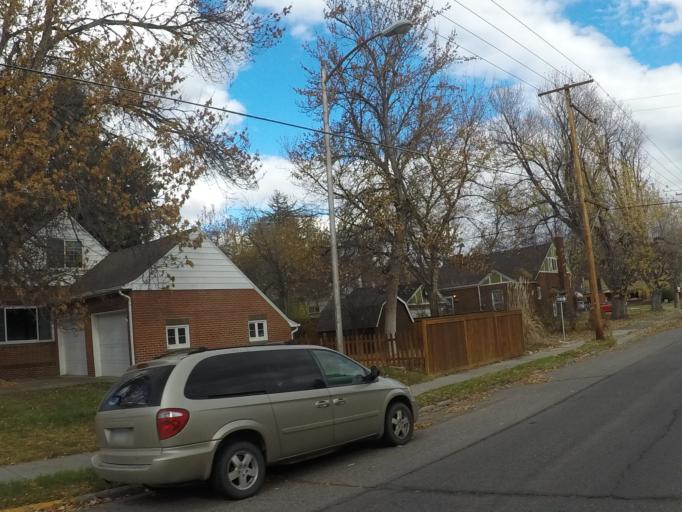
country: US
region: Montana
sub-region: Yellowstone County
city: Billings
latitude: 45.7939
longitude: -108.5245
